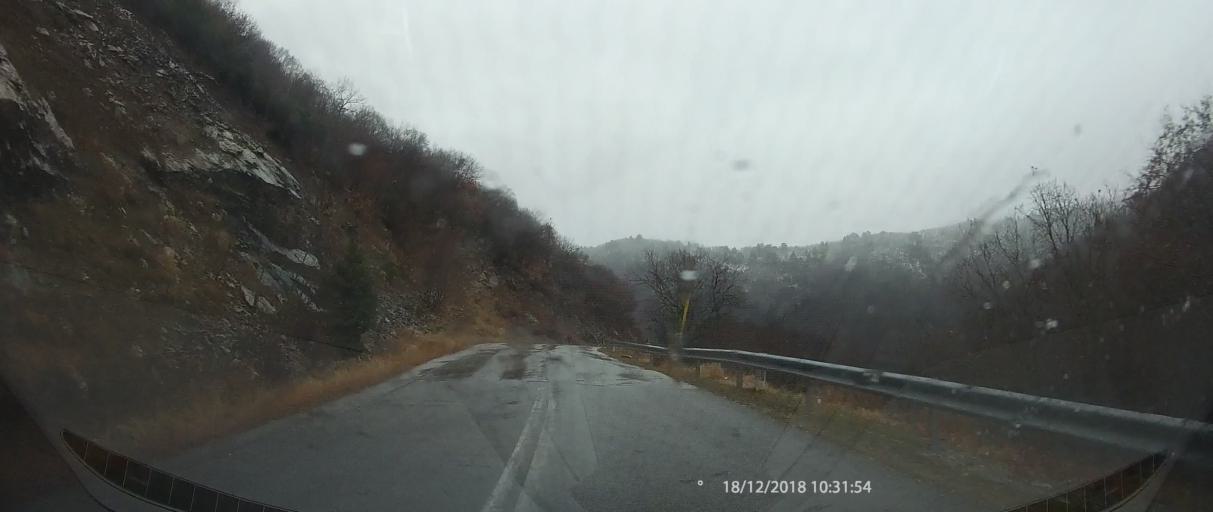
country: GR
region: Central Macedonia
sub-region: Nomos Pierias
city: Kato Milia
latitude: 40.1915
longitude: 22.2875
